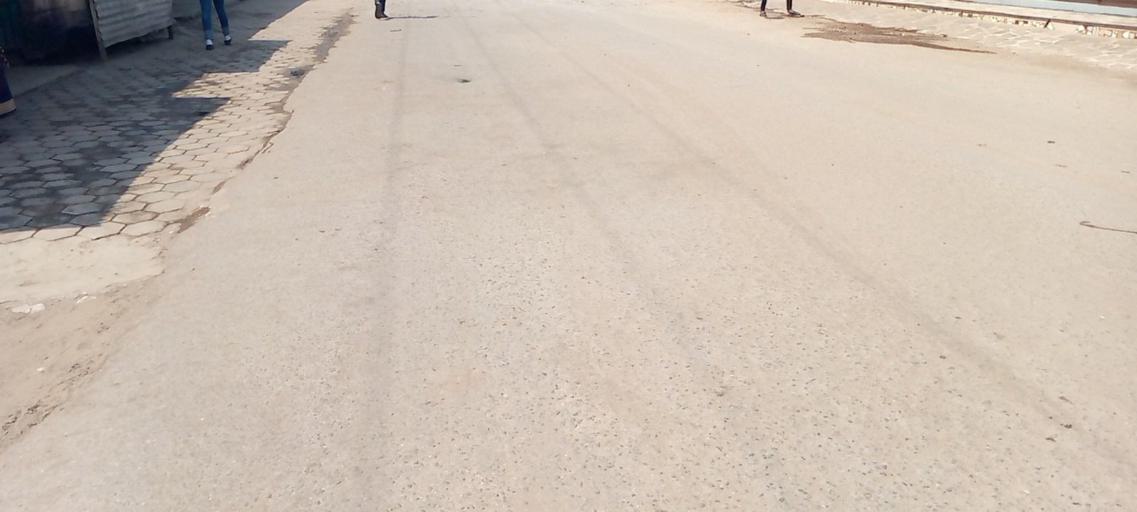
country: ZM
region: Lusaka
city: Lusaka
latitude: -15.4044
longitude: 28.3561
